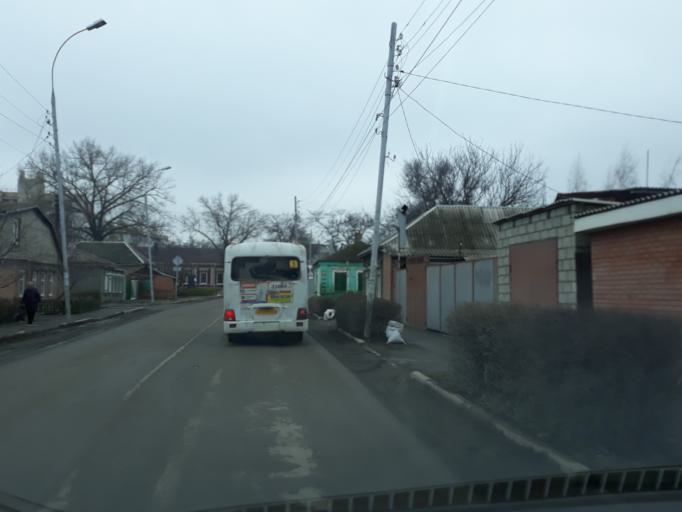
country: RU
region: Rostov
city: Taganrog
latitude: 47.2245
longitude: 38.9238
